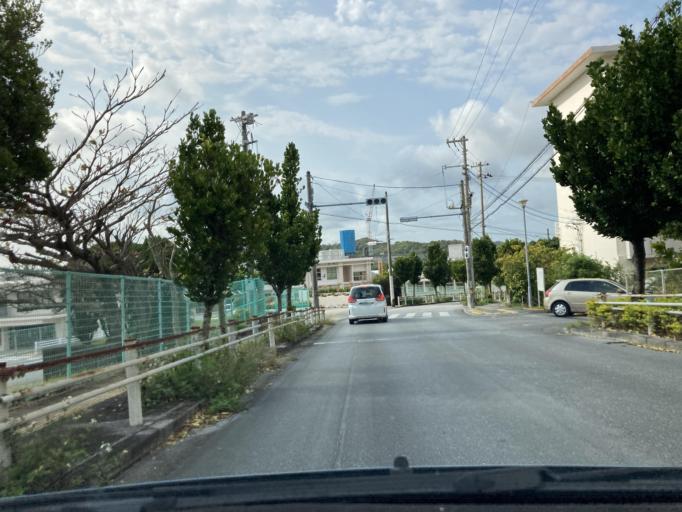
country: JP
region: Okinawa
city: Tomigusuku
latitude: 26.1980
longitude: 127.7212
